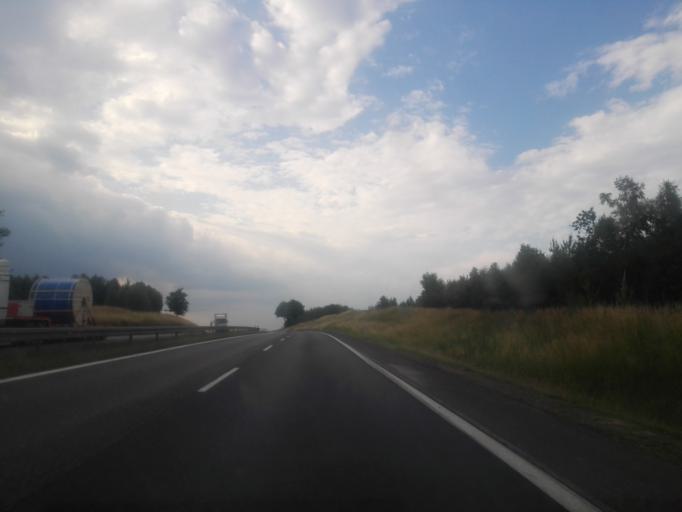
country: PL
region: Silesian Voivodeship
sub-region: Powiat myszkowski
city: Kozieglowy
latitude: 50.5607
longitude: 19.1755
